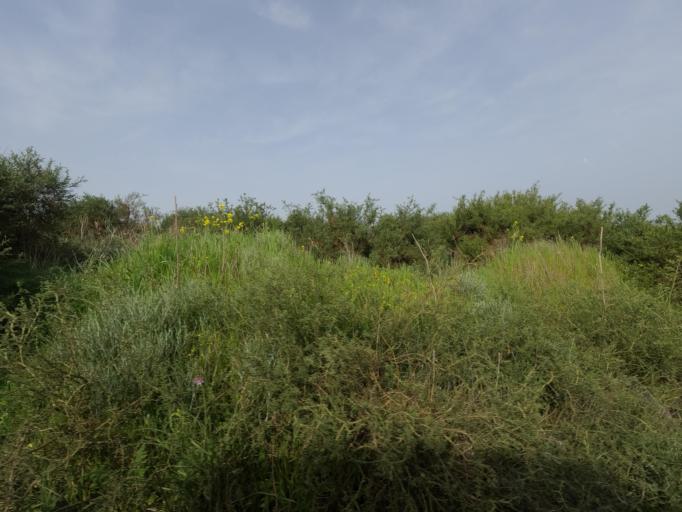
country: CY
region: Pafos
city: Pegeia
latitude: 34.9543
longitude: 32.3784
